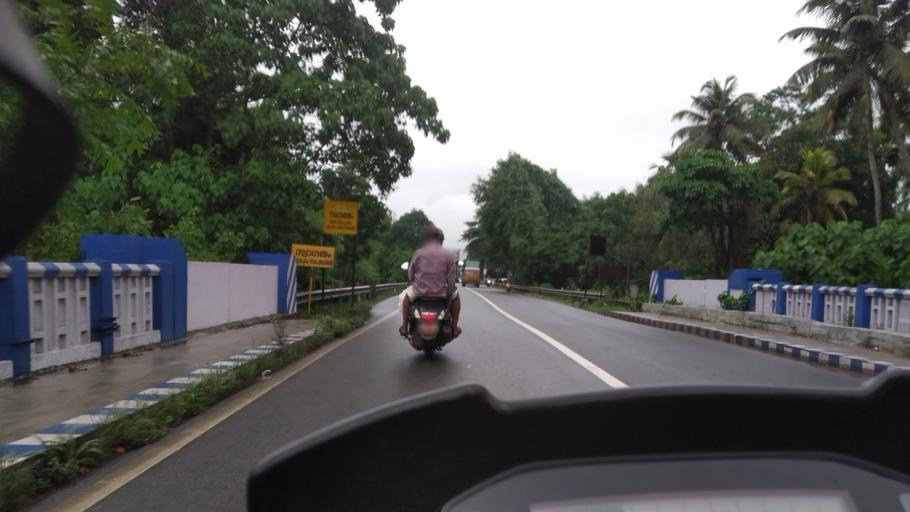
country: IN
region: Kerala
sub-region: Alappuzha
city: Mavelikara
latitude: 9.2822
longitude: 76.4438
